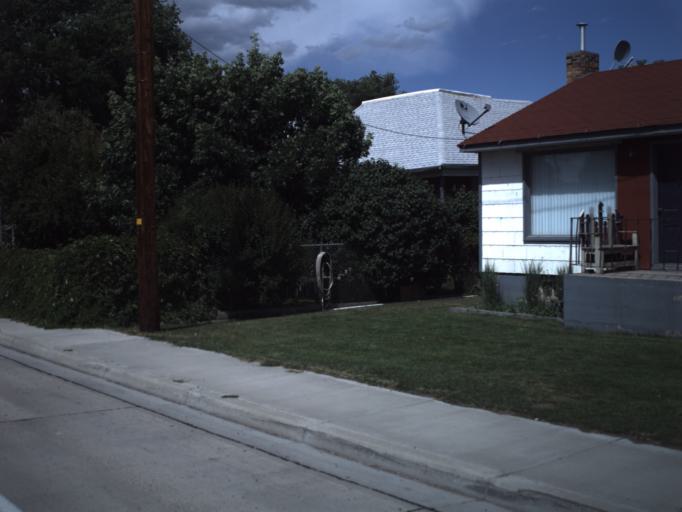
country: US
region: Utah
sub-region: Sevier County
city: Salina
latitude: 38.9612
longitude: -111.8600
